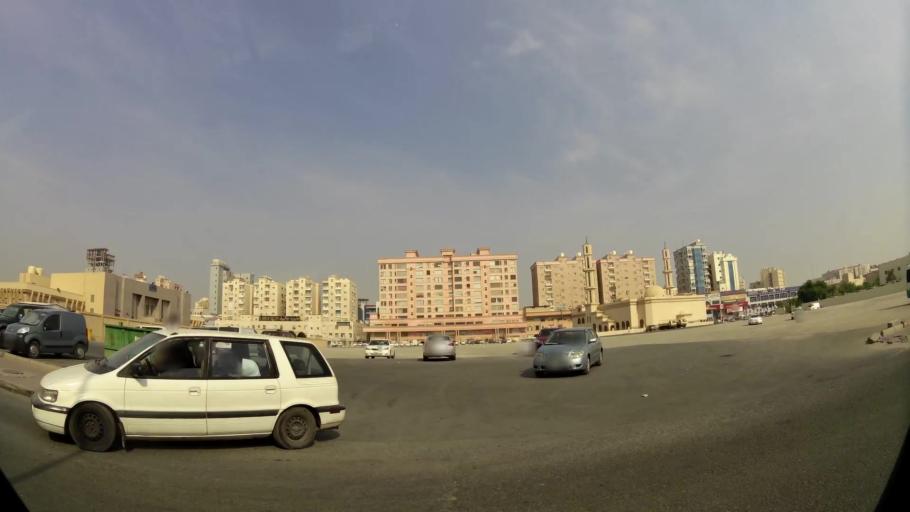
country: KW
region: Al Farwaniyah
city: Al Farwaniyah
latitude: 29.2742
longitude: 47.9605
